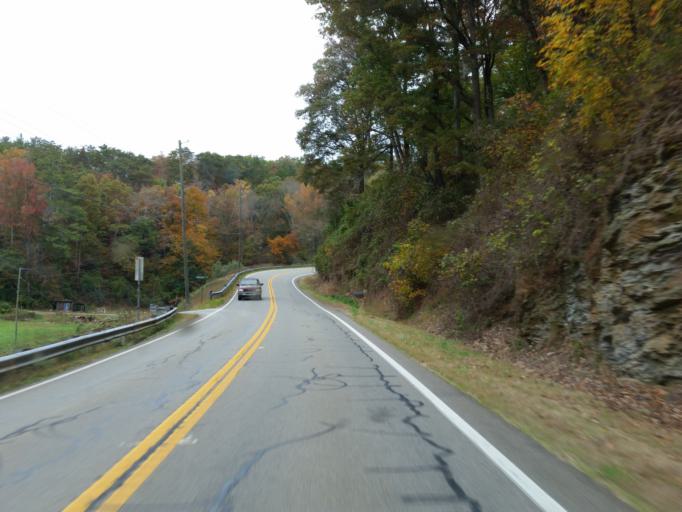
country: US
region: Georgia
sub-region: Pickens County
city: Jasper
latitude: 34.5151
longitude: -84.4356
